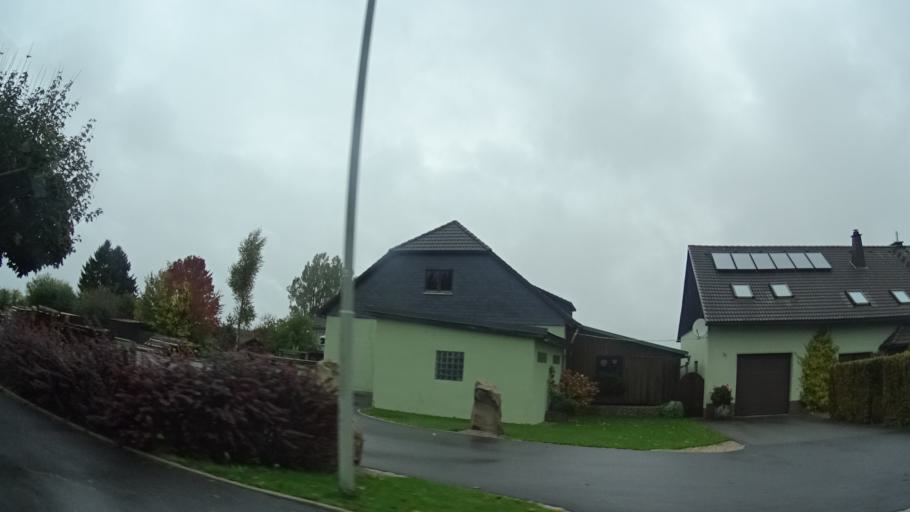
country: DE
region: Bavaria
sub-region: Upper Franconia
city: Tschirn
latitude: 50.3912
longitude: 11.4497
